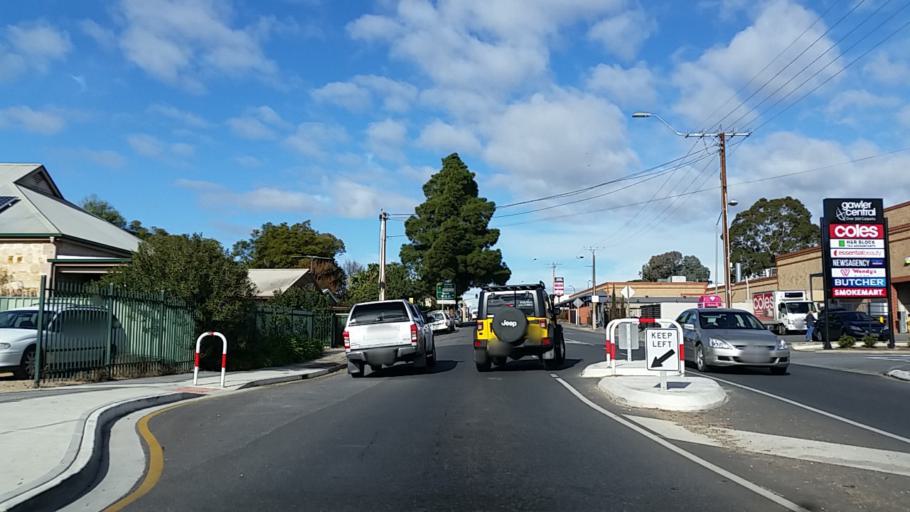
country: AU
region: South Australia
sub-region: Gawler
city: Gawler
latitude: -34.5944
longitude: 138.7490
